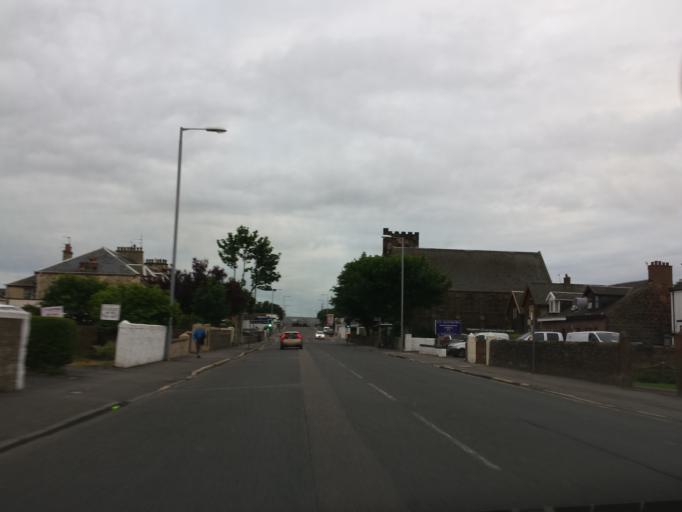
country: GB
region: Scotland
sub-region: South Ayrshire
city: Prestwick
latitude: 55.4748
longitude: -4.6239
